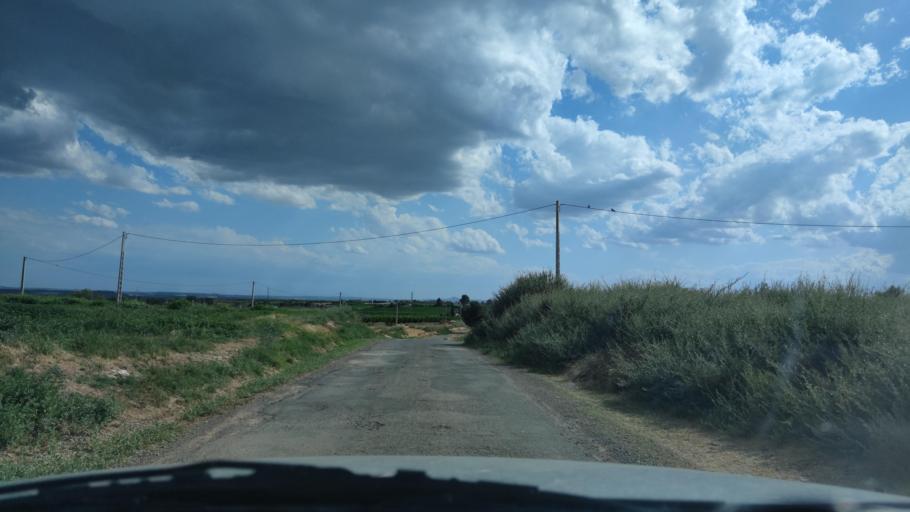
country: ES
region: Catalonia
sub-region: Provincia de Lleida
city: Alcarras
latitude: 41.5893
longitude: 0.5387
